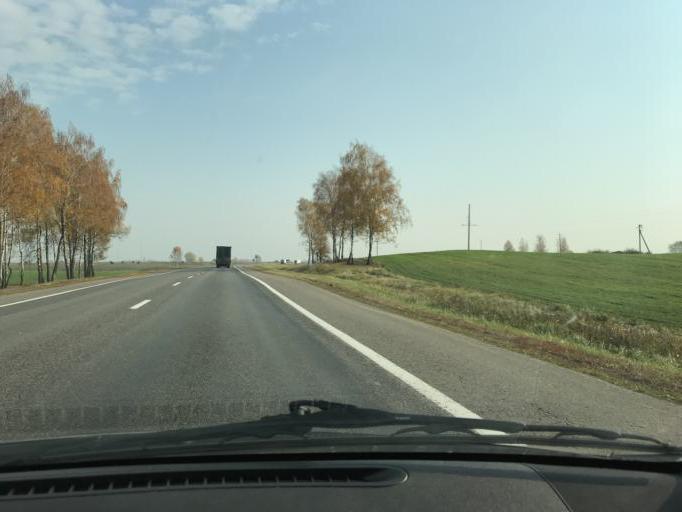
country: BY
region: Vitebsk
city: Chashniki
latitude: 55.0136
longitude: 29.1095
